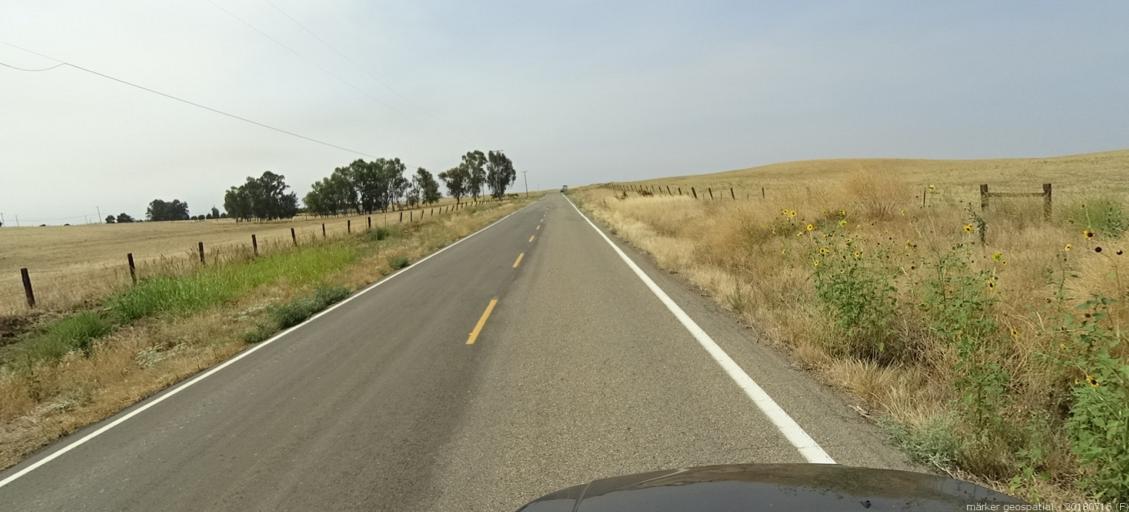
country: US
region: California
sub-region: Madera County
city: Bonadelle Ranchos-Madera Ranchos
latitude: 37.1061
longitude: -119.9408
